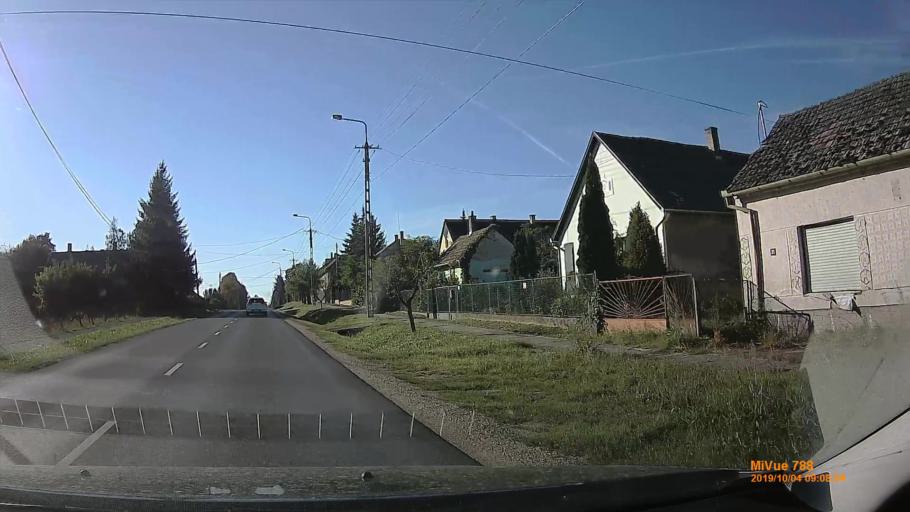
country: HU
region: Somogy
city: Karad
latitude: 46.6736
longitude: 17.7762
